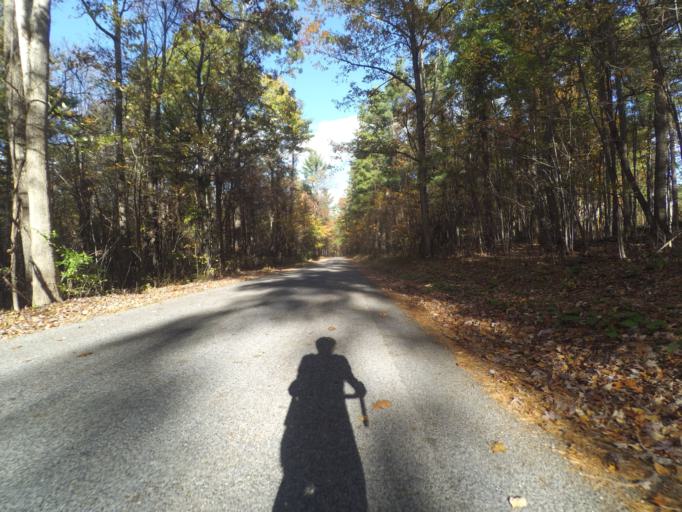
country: US
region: Pennsylvania
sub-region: Centre County
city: Houserville
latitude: 40.8677
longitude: -77.8186
